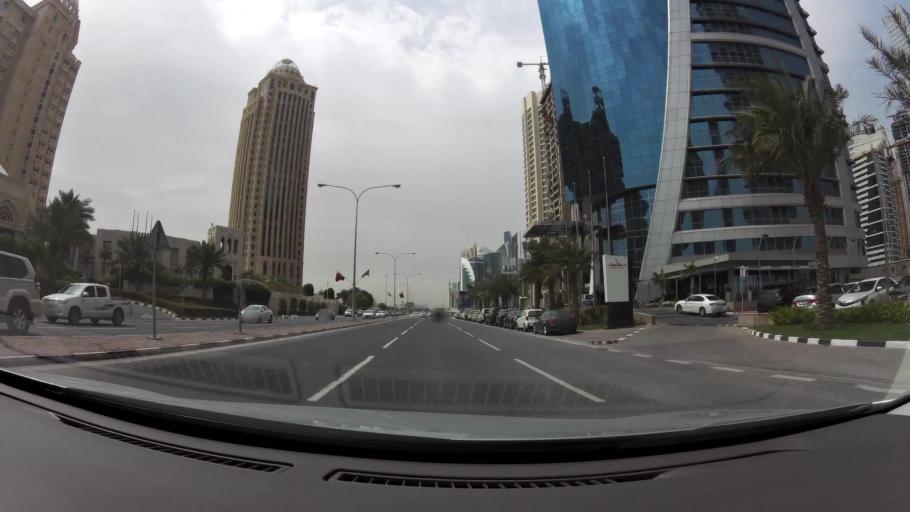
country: QA
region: Baladiyat ad Dawhah
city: Doha
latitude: 25.3252
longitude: 51.5385
